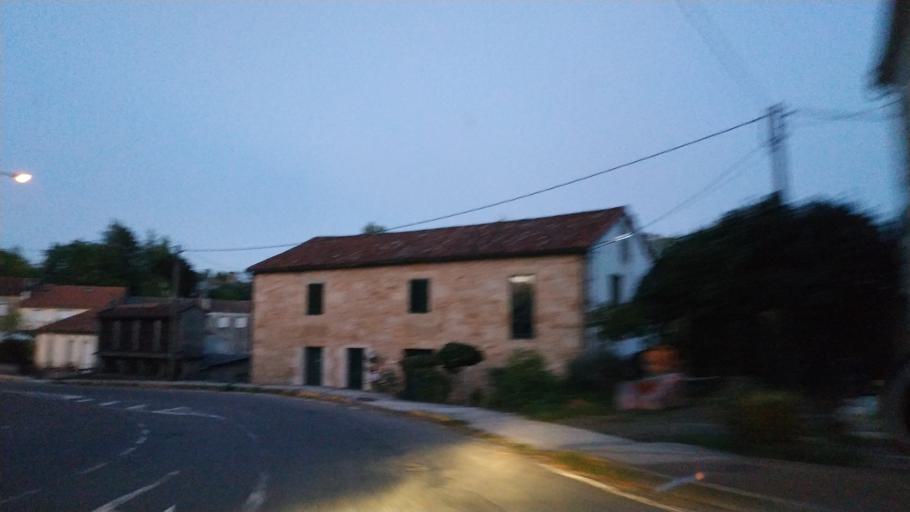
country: ES
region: Galicia
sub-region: Provincia da Coruna
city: Negreira
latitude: 42.9063
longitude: -8.7405
